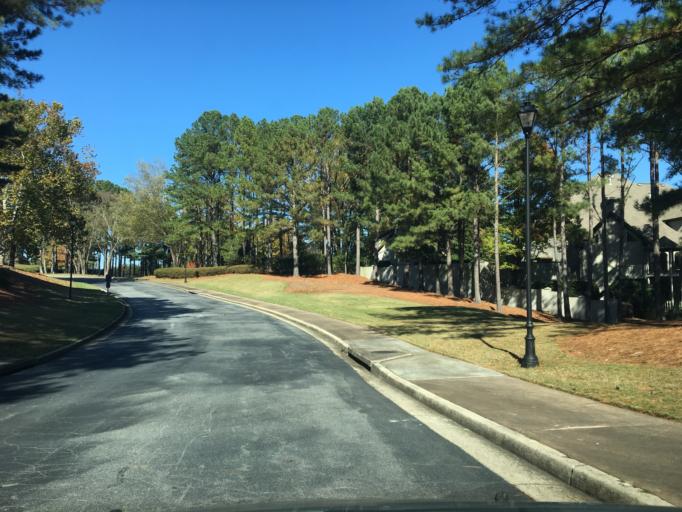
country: US
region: Georgia
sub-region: Fulton County
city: Johns Creek
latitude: 34.0292
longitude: -84.1832
